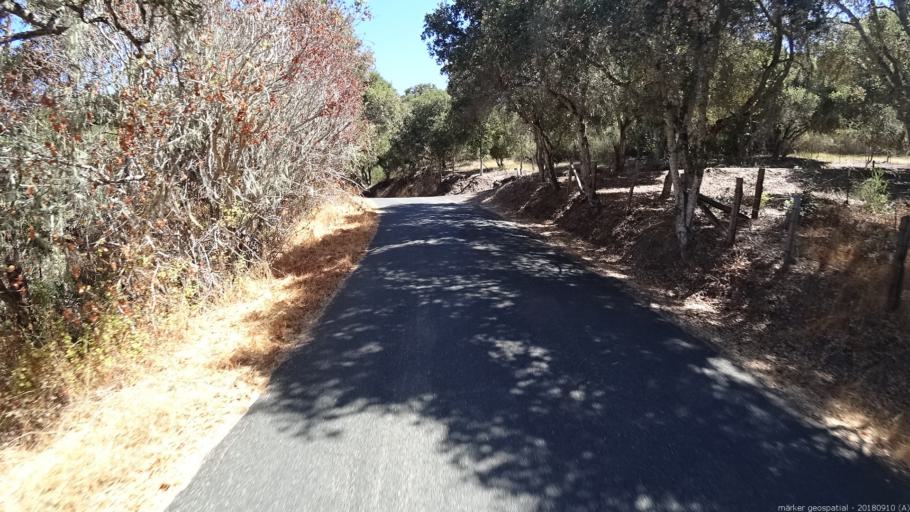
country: US
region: California
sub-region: Monterey County
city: Carmel Valley Village
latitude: 36.5037
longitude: -121.8087
